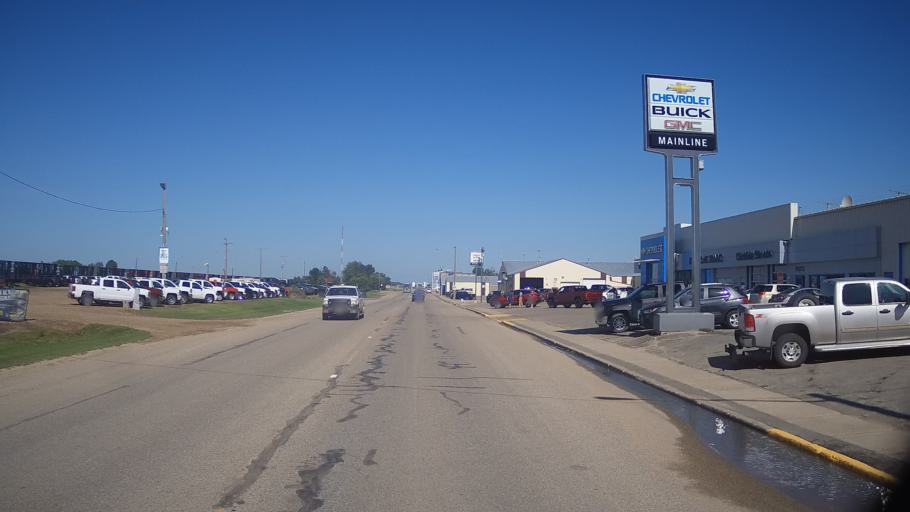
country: CA
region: Saskatchewan
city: Watrous
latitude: 51.6705
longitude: -105.4647
